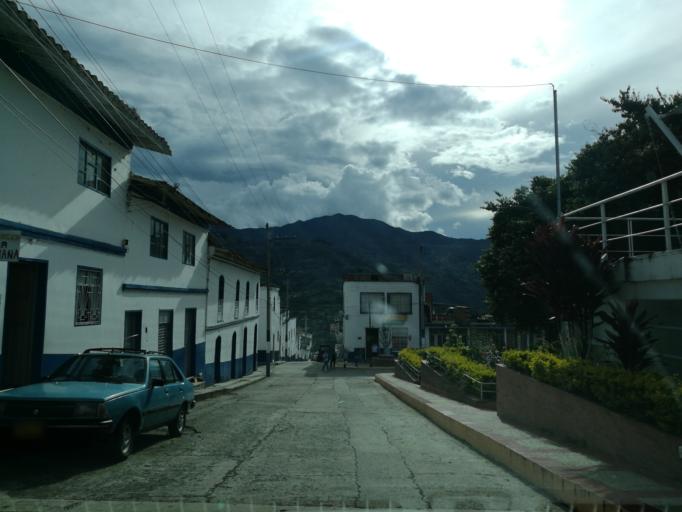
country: CO
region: Boyaca
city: El Espino
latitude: 6.4827
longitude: -72.4961
